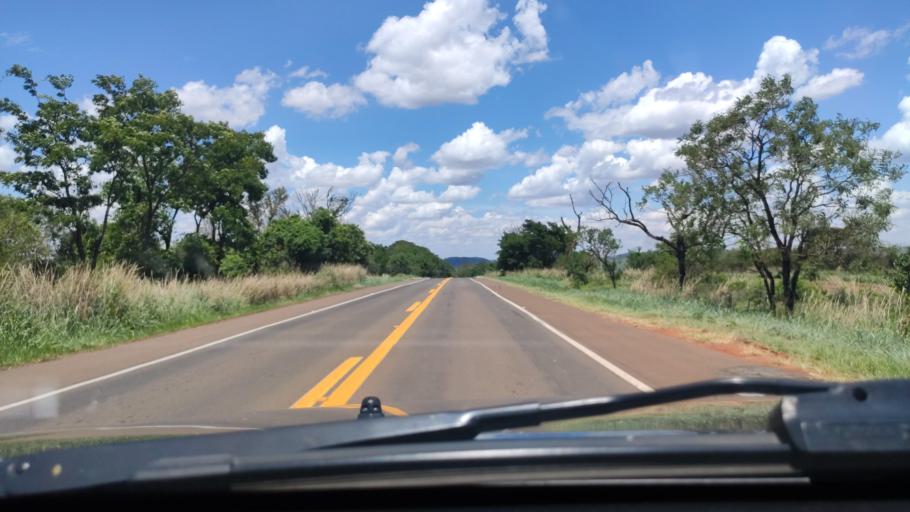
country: BR
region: Sao Paulo
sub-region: Boa Esperanca Do Sul
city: Boa Esperanca do Sul
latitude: -22.0696
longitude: -48.4085
